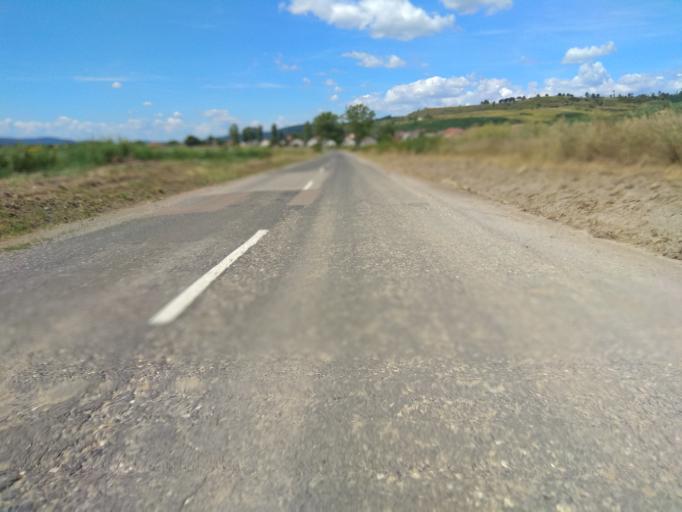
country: HU
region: Borsod-Abauj-Zemplen
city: Sajokaza
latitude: 48.2878
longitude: 20.6050
